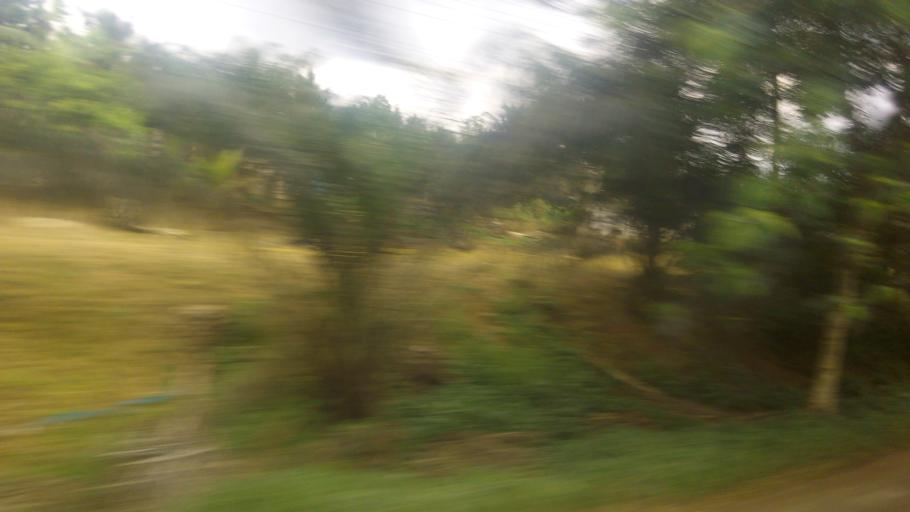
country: GH
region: Western
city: Takoradi
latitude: 4.8957
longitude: -1.9342
